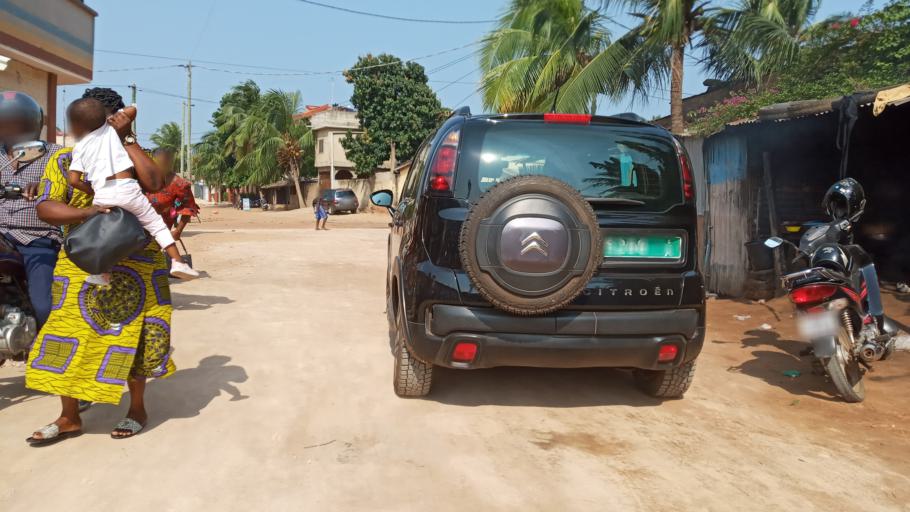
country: TG
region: Maritime
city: Lome
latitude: 6.2059
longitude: 1.1846
